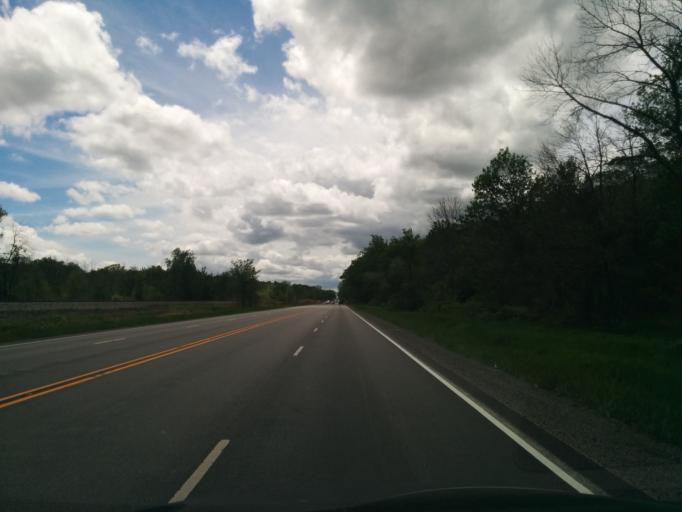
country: US
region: Indiana
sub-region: LaPorte County
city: Michigan City
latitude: 41.6688
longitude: -86.9781
